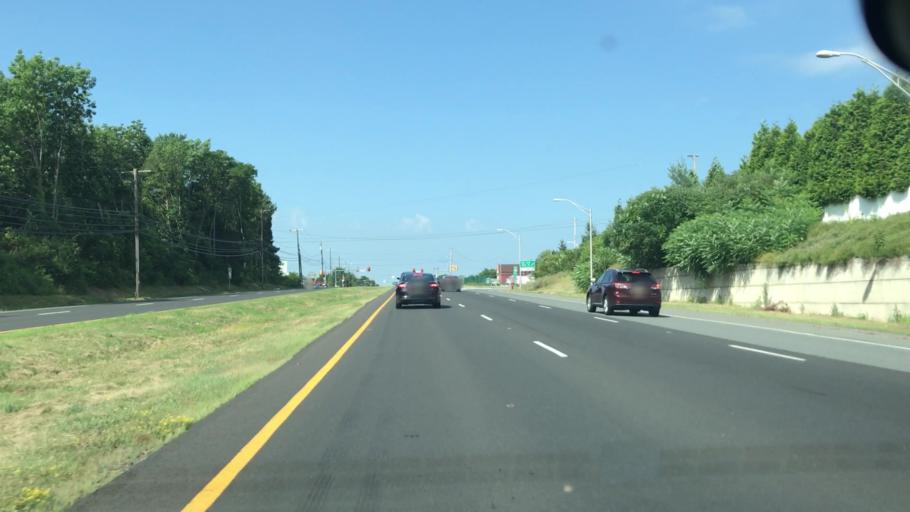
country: US
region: New Jersey
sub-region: Hunterdon County
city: Flemington
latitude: 40.5140
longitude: -74.8254
